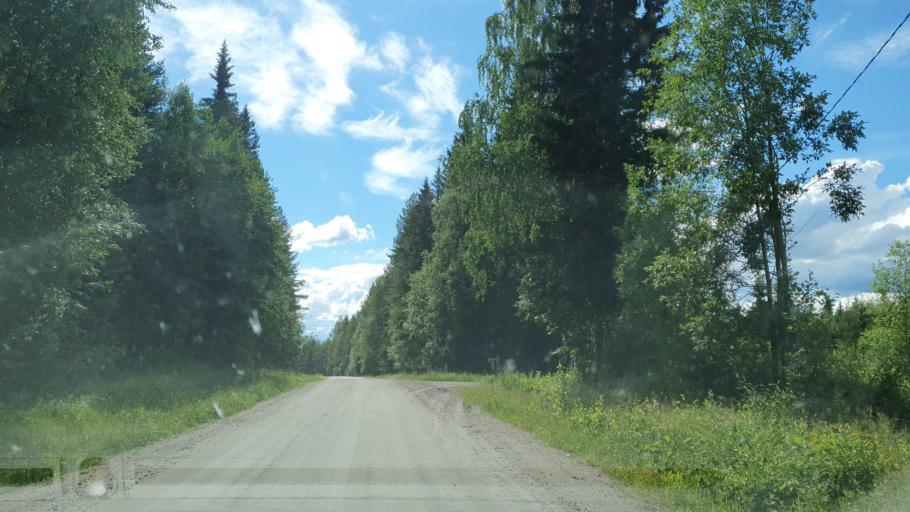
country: FI
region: Kainuu
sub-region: Kehys-Kainuu
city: Kuhmo
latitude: 64.1656
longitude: 29.8626
